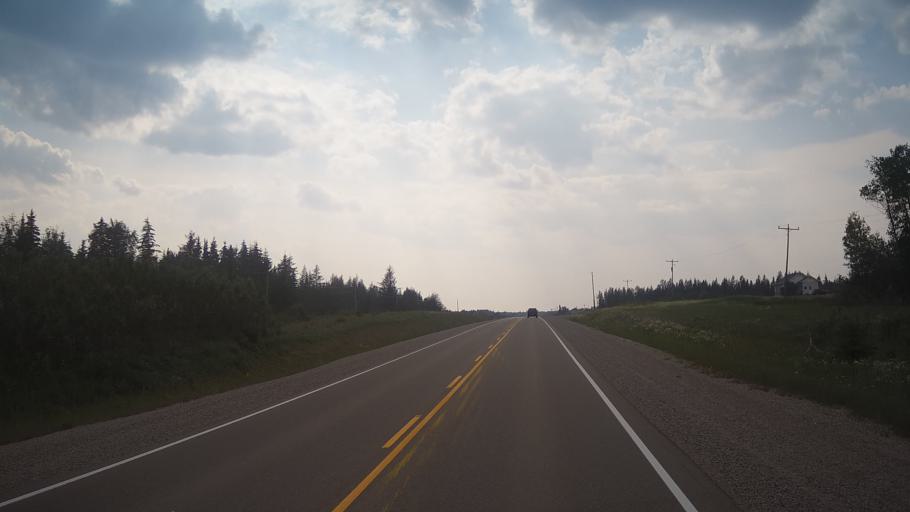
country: CA
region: Ontario
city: Kapuskasing
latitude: 49.4640
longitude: -82.6265
